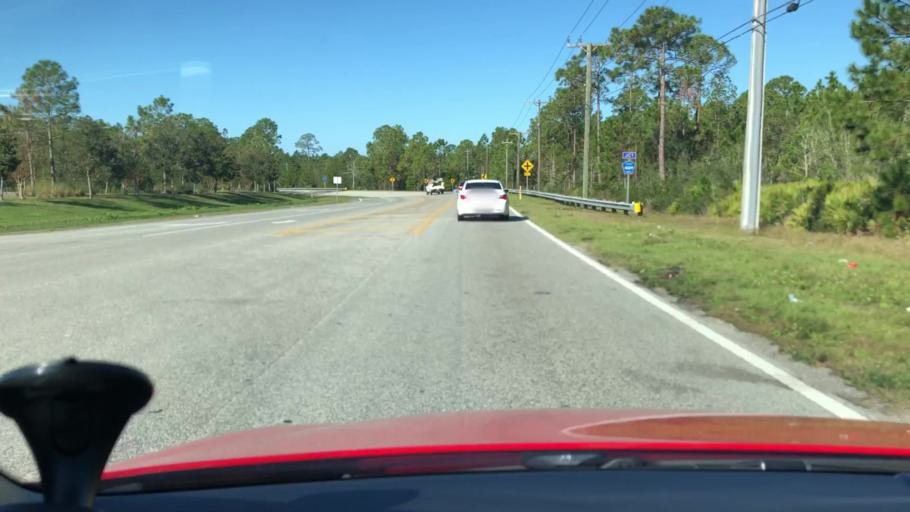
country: US
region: Florida
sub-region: Volusia County
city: Holly Hill
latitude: 29.2139
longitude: -81.0869
